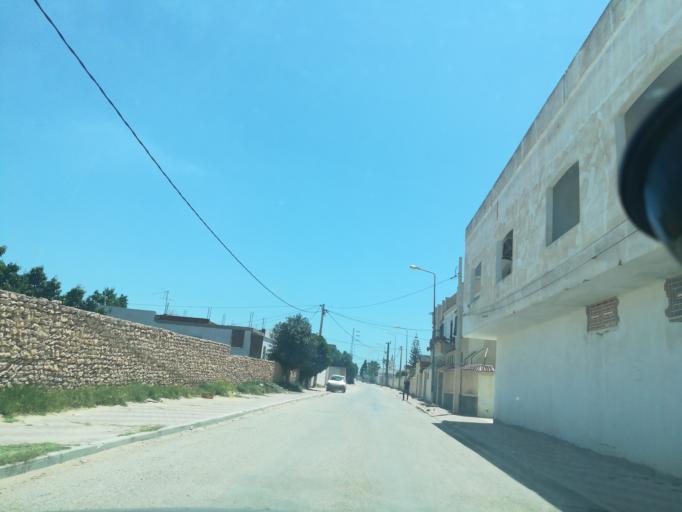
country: TN
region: Safaqis
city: Al Qarmadah
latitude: 34.8230
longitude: 10.7553
